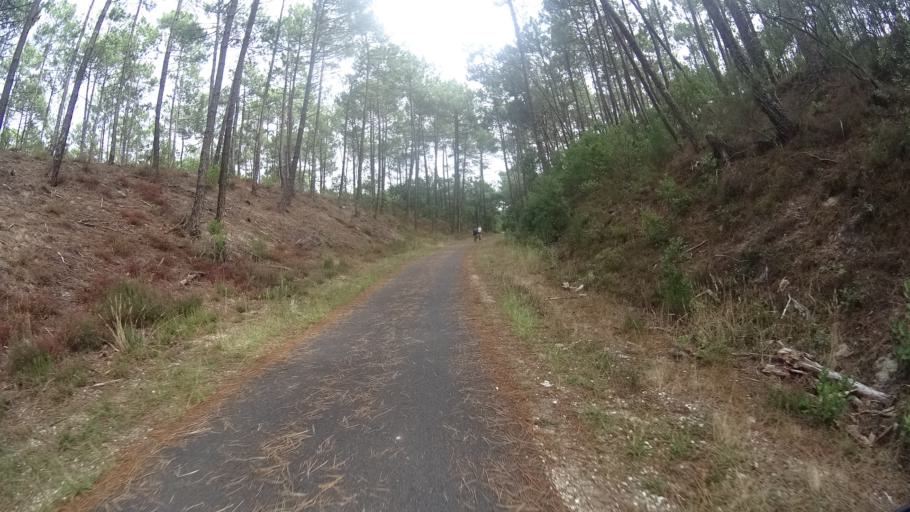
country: FR
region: Aquitaine
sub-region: Departement de la Gironde
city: Lacanau
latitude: 45.0057
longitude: -1.1394
